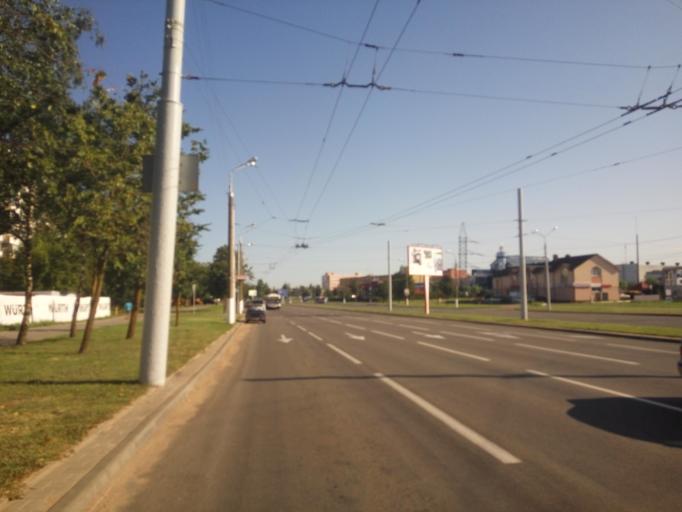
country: BY
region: Vitebsk
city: Vitebsk
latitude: 55.1887
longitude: 30.2492
